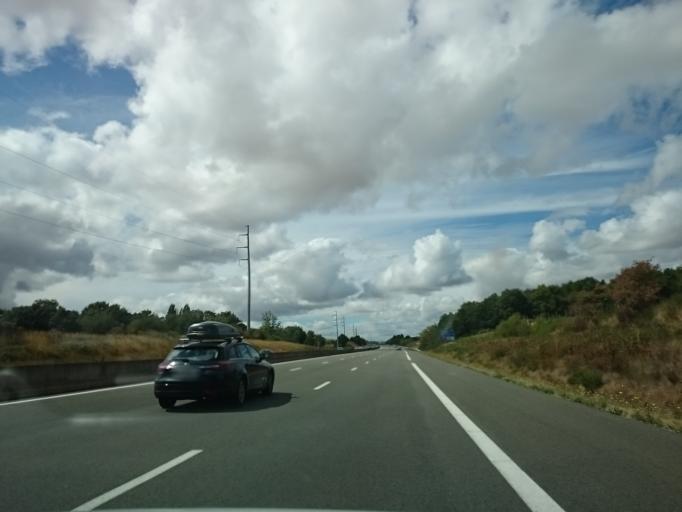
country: FR
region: Centre
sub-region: Departement d'Eure-et-Loir
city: Yevres
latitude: 48.2832
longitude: 1.2370
